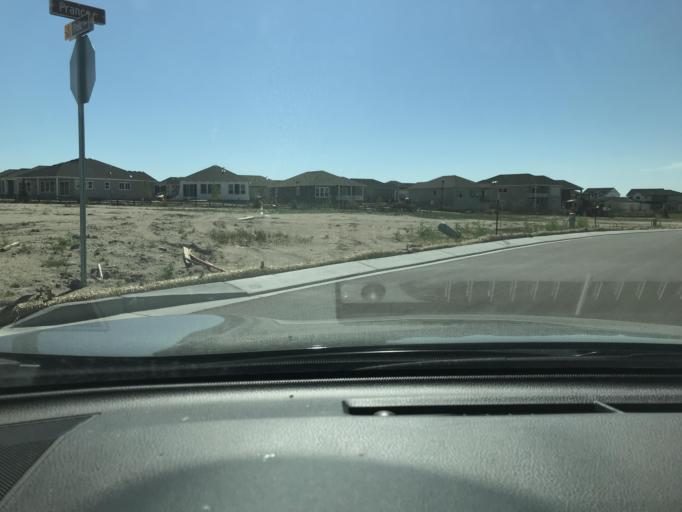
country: US
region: Colorado
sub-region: El Paso County
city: Black Forest
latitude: 38.9647
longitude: -104.7061
